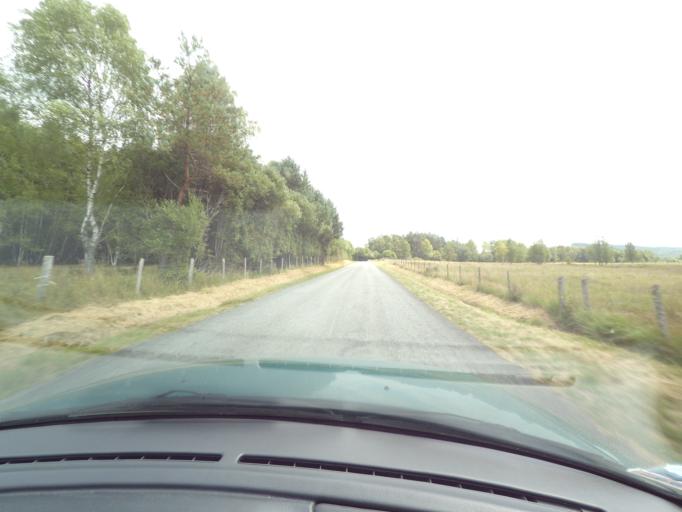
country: FR
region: Limousin
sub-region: Departement de la Correze
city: Bugeat
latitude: 45.7041
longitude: 2.0325
